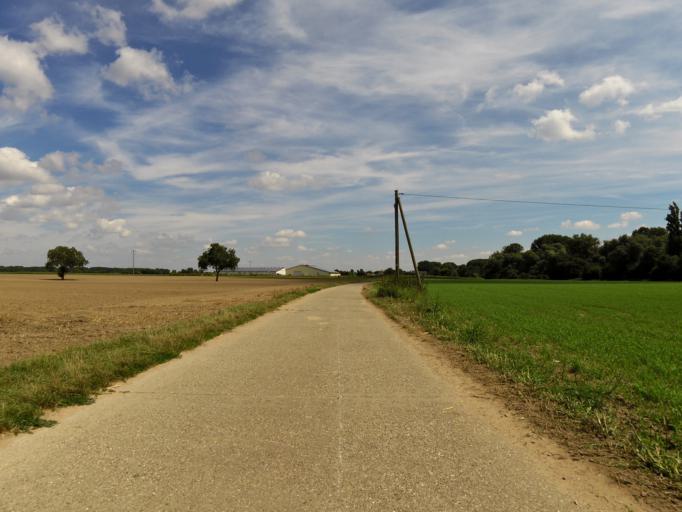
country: DE
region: Rheinland-Pfalz
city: Rulzheim
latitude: 49.1633
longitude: 8.3047
